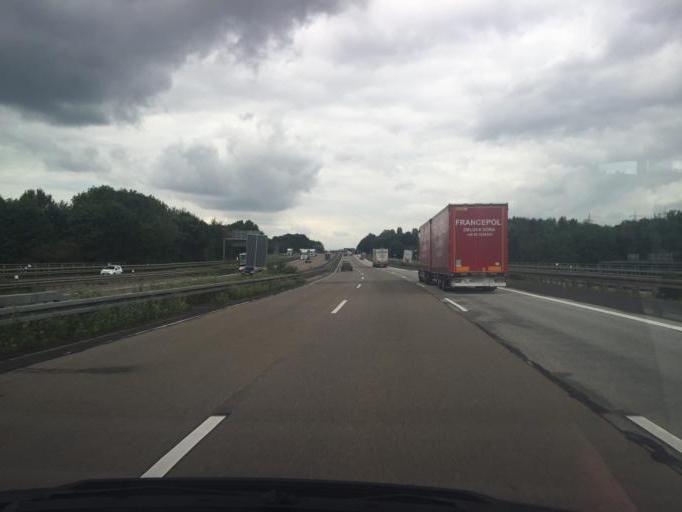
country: DE
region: Hesse
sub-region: Regierungsbezirk Giessen
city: Limburg an der Lahn
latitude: 50.3991
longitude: 8.0718
